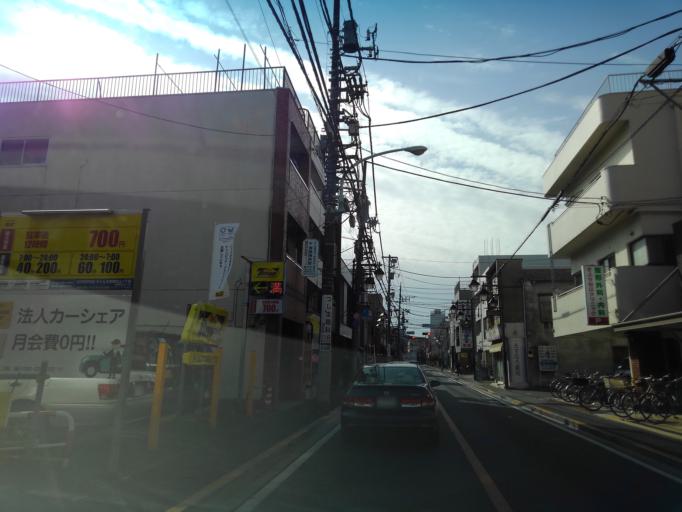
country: JP
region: Tokyo
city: Tanashicho
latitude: 35.7701
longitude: 139.5169
